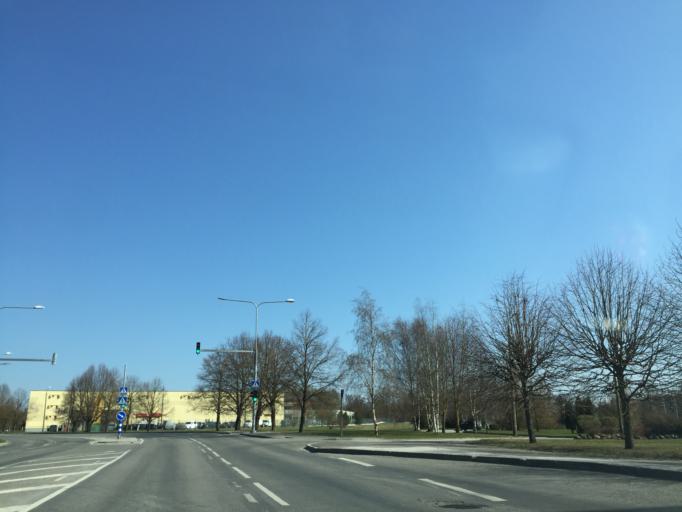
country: EE
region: Tartu
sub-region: Tartu linn
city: Tartu
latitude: 58.3762
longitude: 26.7705
